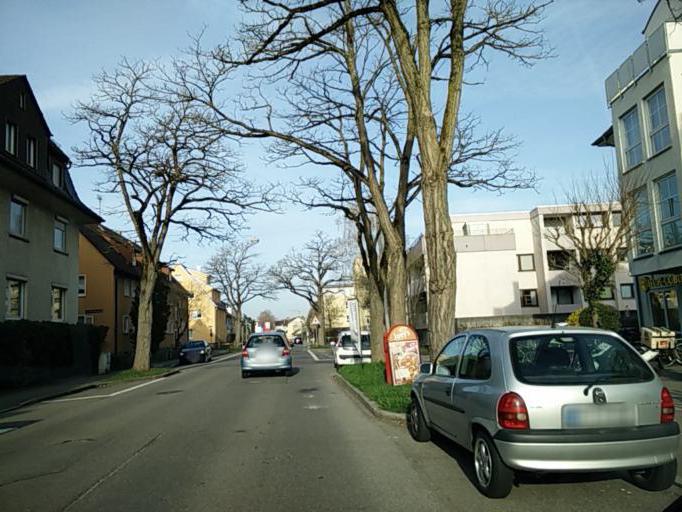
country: DE
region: Baden-Wuerttemberg
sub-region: Tuebingen Region
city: Tuebingen
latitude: 48.5239
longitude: 9.0426
